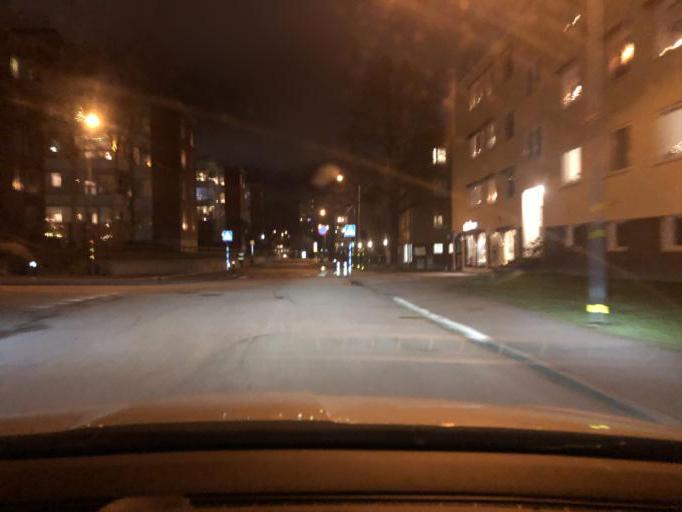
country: SE
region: Vaermland
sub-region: Karlstads Kommun
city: Karlstad
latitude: 59.3757
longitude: 13.4882
